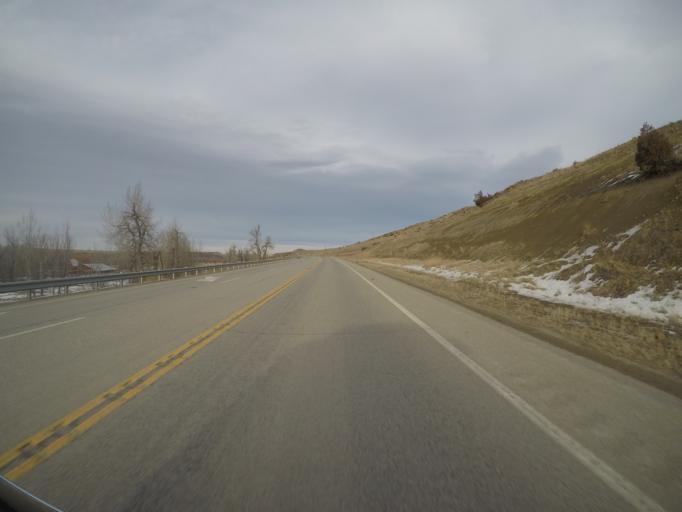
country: US
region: Montana
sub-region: Stillwater County
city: Absarokee
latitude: 45.4935
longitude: -109.4510
